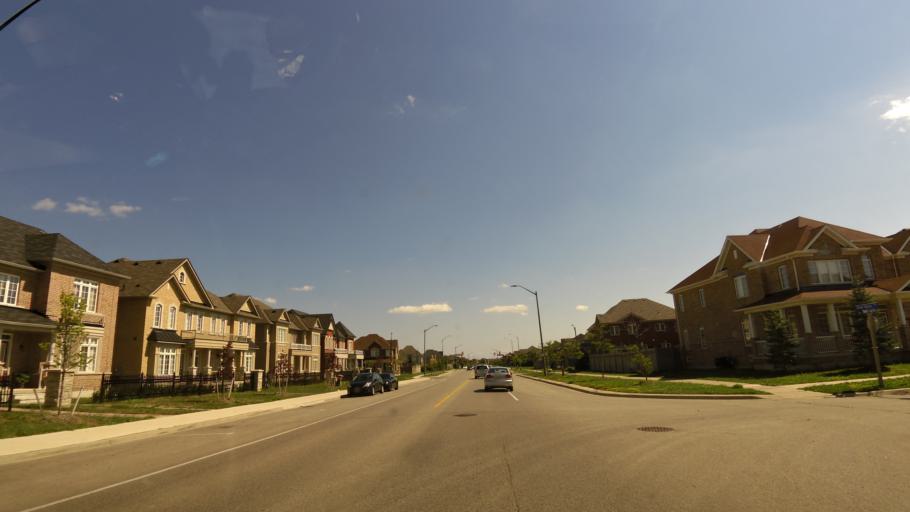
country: CA
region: Ontario
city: Mississauga
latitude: 43.5535
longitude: -79.7344
